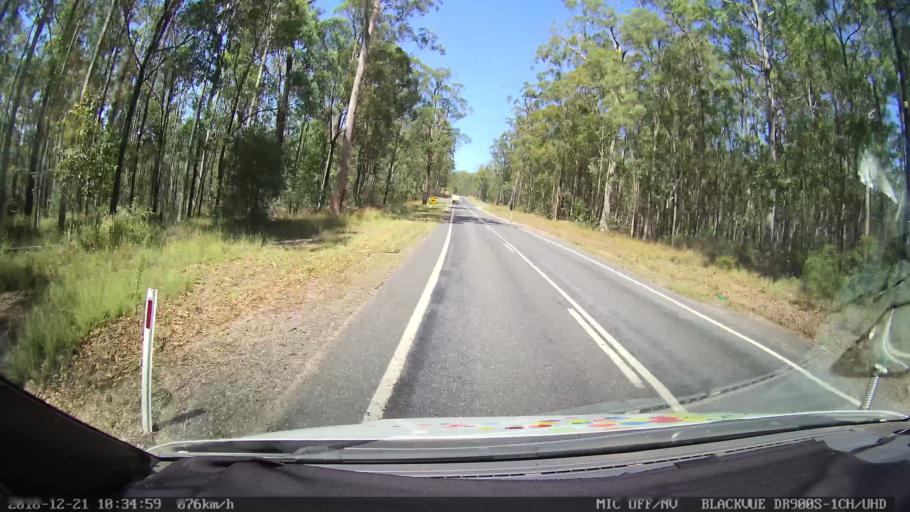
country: AU
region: New South Wales
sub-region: Clarence Valley
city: South Grafton
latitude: -29.6168
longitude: 152.6487
